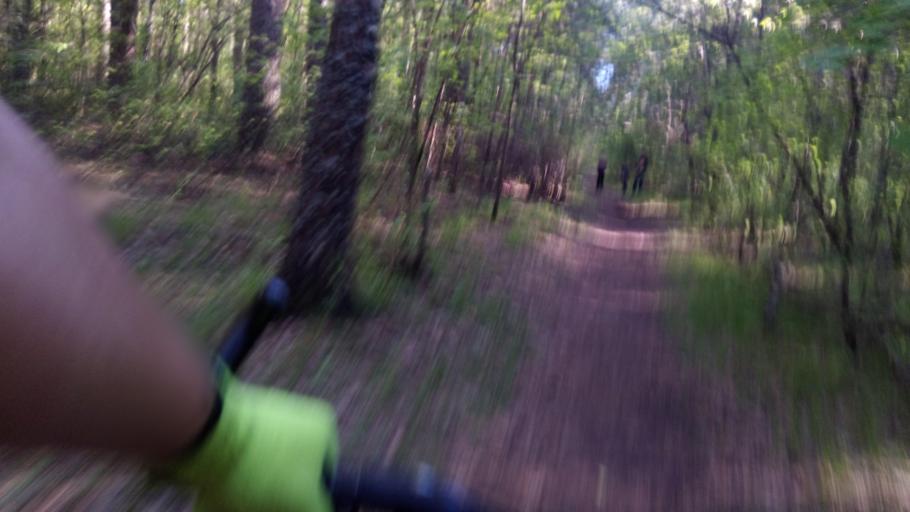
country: RU
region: Chelyabinsk
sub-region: Gorod Chelyabinsk
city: Chelyabinsk
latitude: 55.1508
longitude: 61.3474
